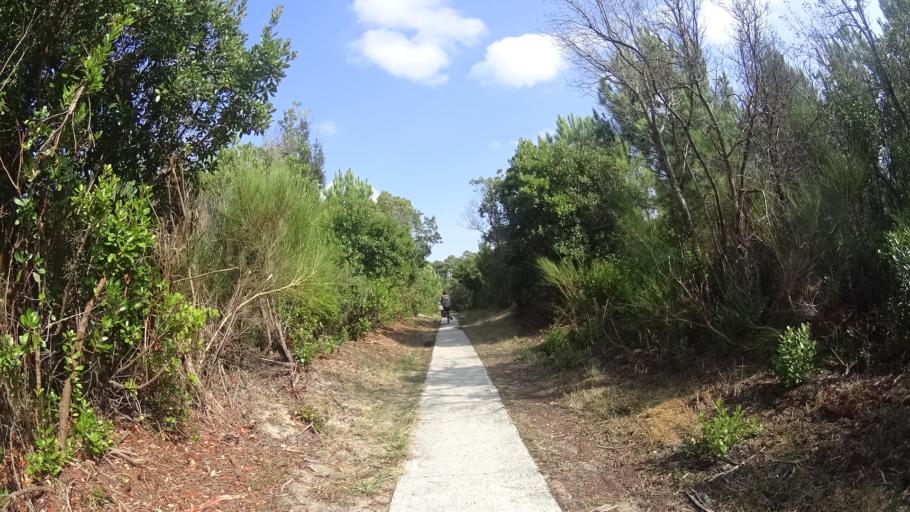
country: FR
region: Aquitaine
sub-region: Departement de la Gironde
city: Lacanau
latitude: 44.9655
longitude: -1.1764
